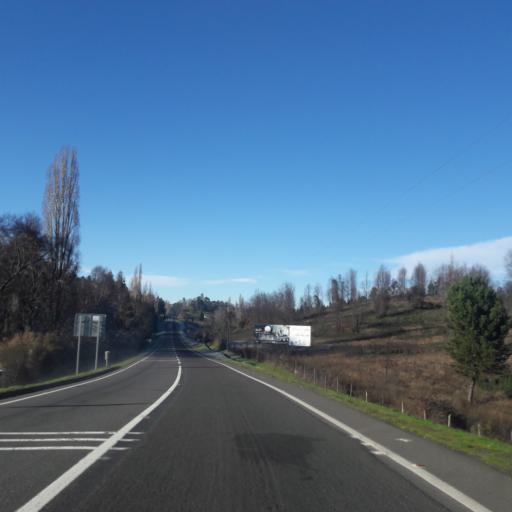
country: CL
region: Biobio
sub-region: Provincia de Biobio
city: La Laja
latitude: -37.3185
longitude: -72.9214
